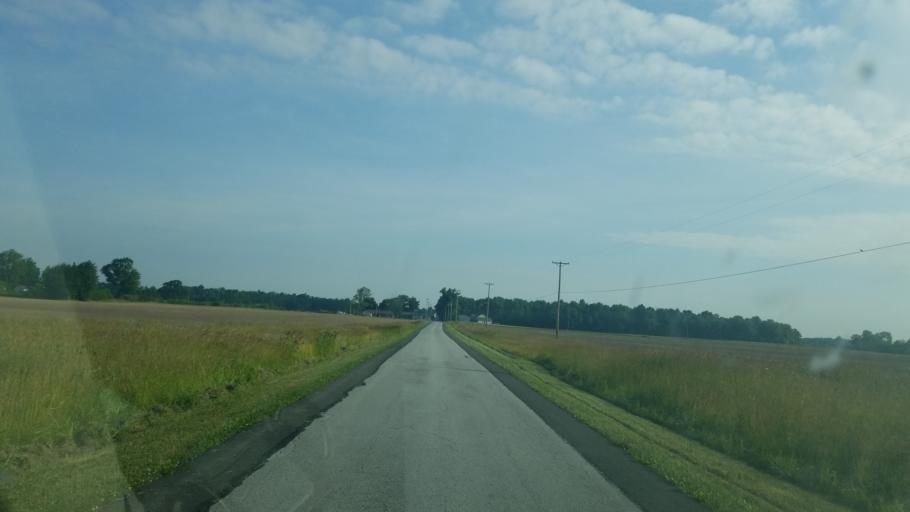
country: US
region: Ohio
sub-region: Hancock County
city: Arlington
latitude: 40.8303
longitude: -83.6704
